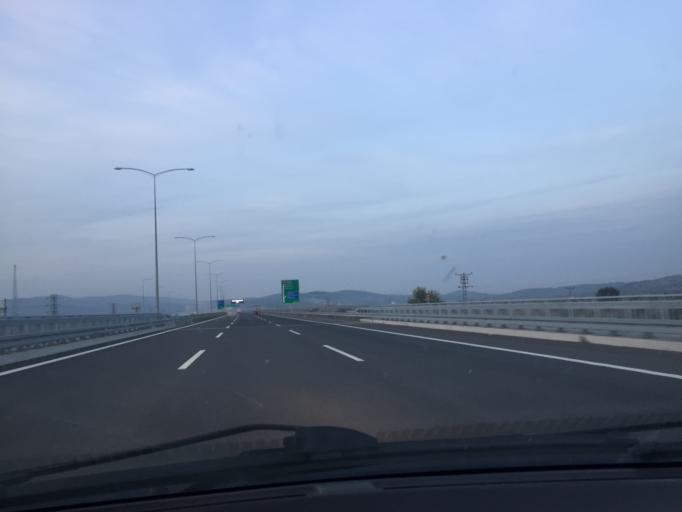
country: TR
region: Manisa
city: Halitpasa
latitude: 38.7581
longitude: 27.6603
